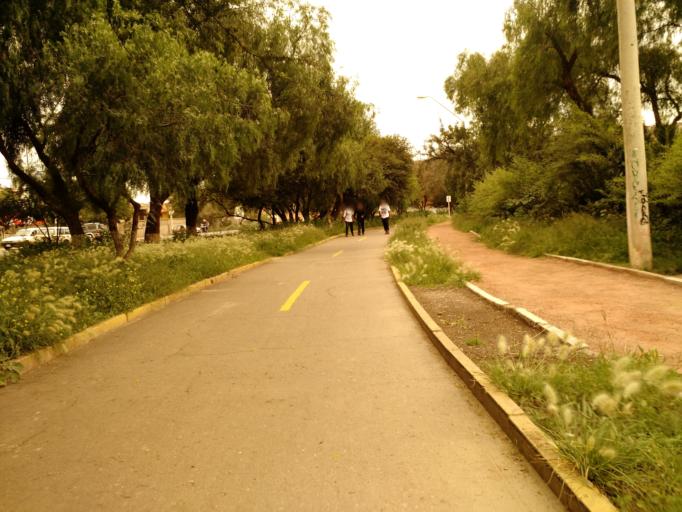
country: BO
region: Cochabamba
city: Cochabamba
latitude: -17.4158
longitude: -66.1263
